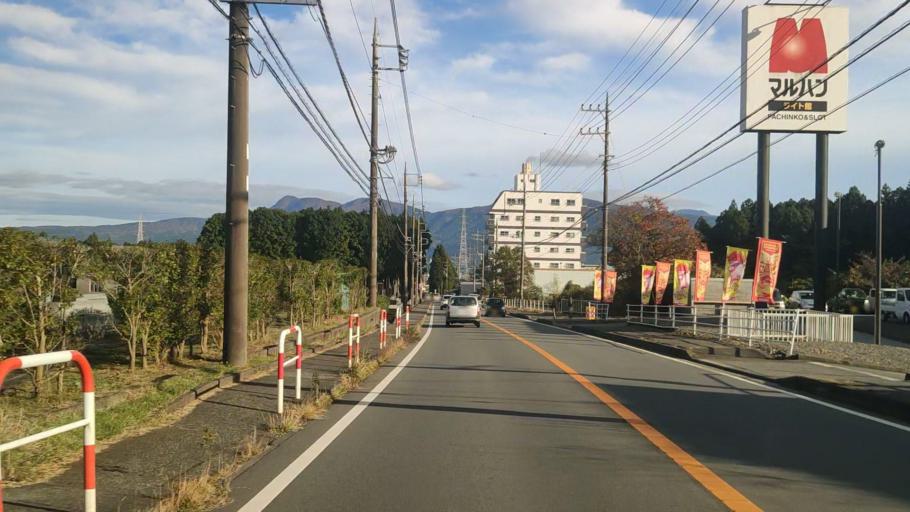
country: JP
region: Shizuoka
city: Gotemba
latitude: 35.3092
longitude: 138.9088
